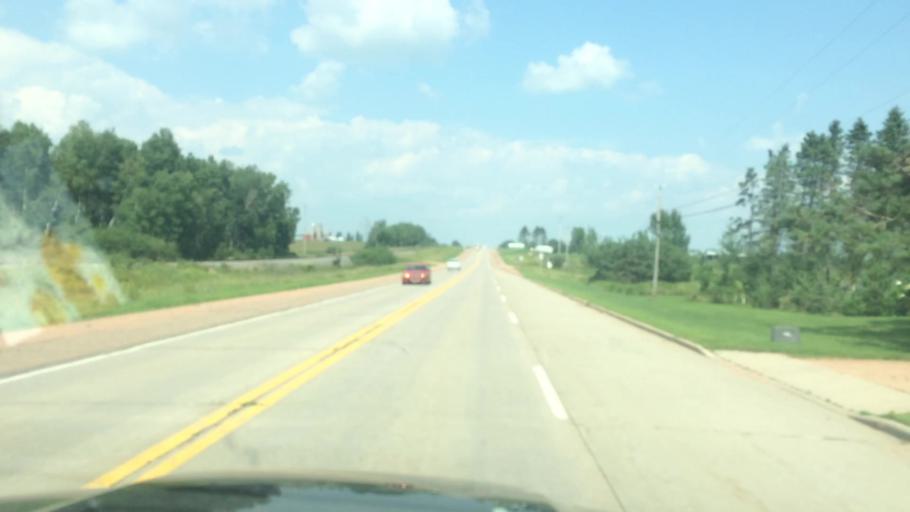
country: US
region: Wisconsin
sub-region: Clark County
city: Colby
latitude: 44.8571
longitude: -90.3158
